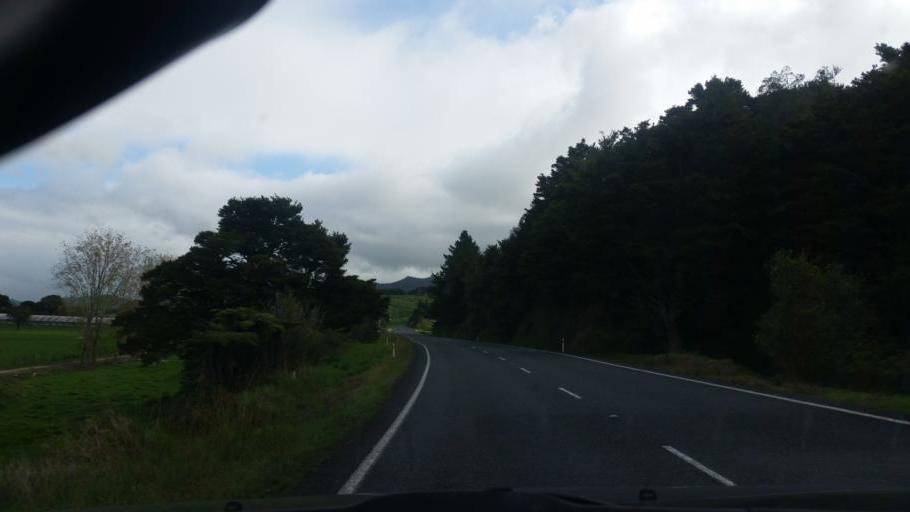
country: NZ
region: Northland
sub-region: Whangarei
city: Maungatapere
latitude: -35.8191
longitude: 174.0349
